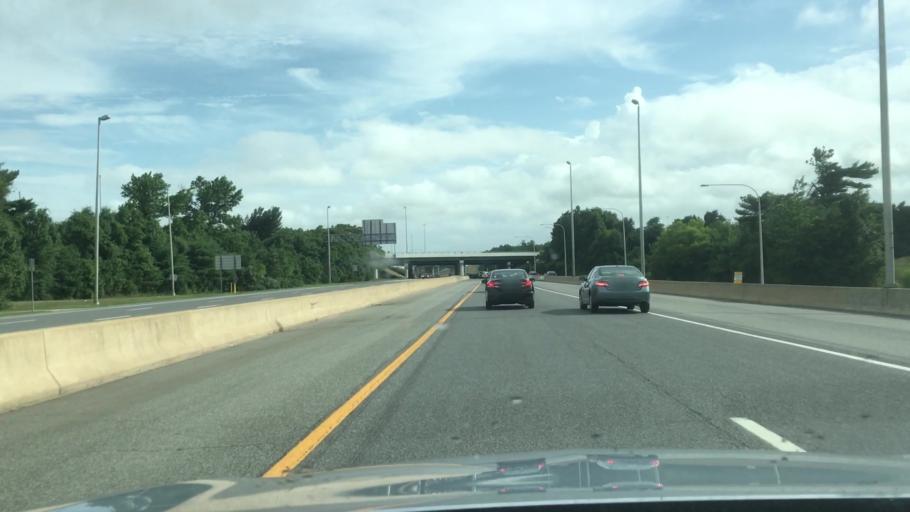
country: US
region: Delaware
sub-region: New Castle County
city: Newport
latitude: 39.6868
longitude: -75.6555
